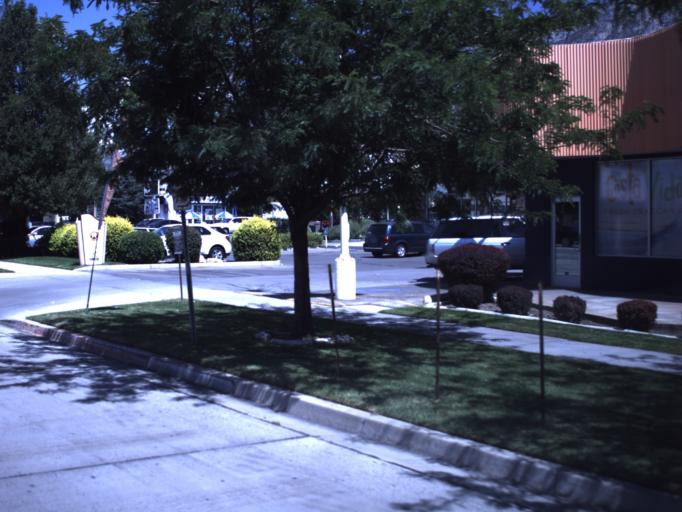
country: US
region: Utah
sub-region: Utah County
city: Provo
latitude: 40.2500
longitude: -111.6585
